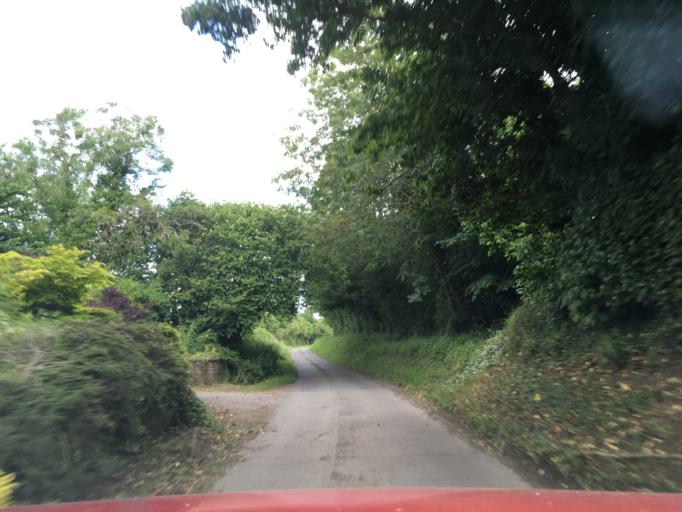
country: GB
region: England
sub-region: Gloucestershire
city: Coates
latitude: 51.6596
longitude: -2.0217
